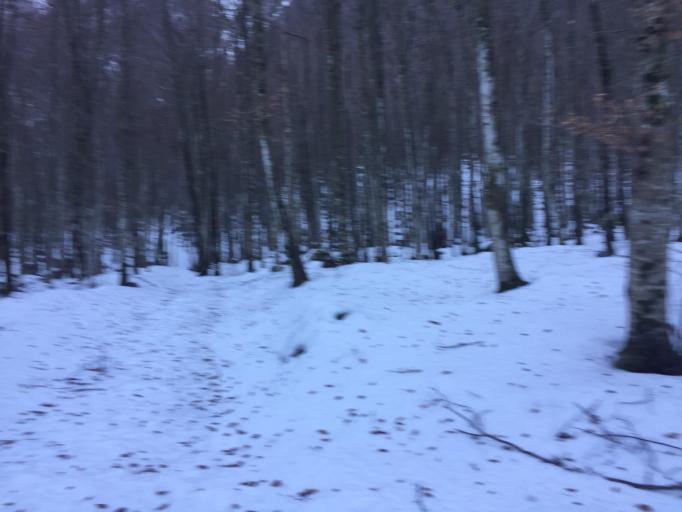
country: IT
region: Friuli Venezia Giulia
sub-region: Provincia di Udine
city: Prato
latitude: 46.3446
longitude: 13.2900
